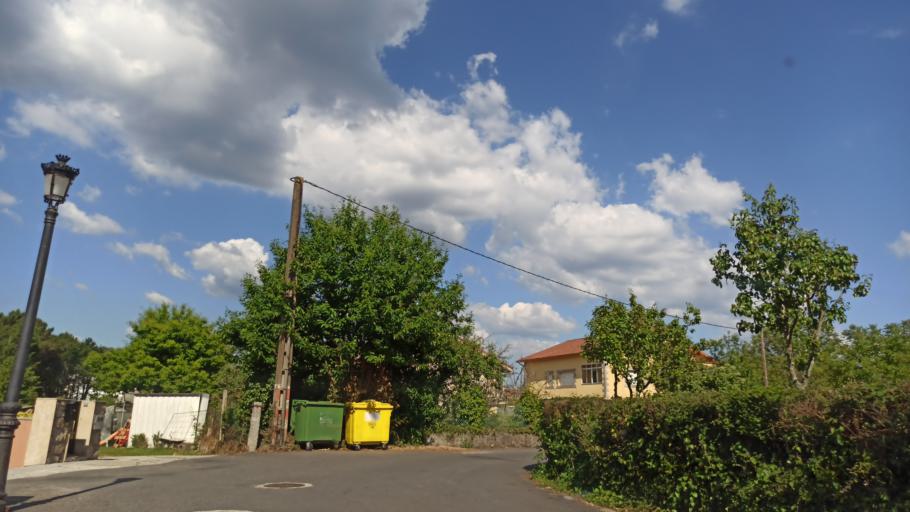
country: ES
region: Galicia
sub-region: Provincia da Coruna
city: Negreira
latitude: 42.9141
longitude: -8.7392
